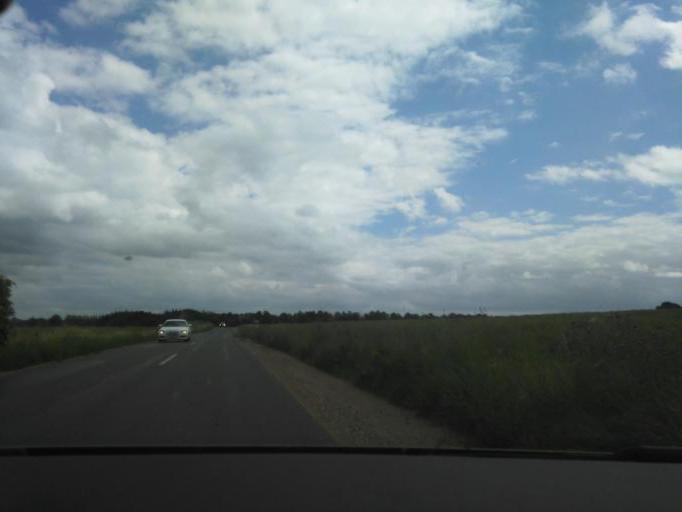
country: DK
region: Zealand
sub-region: Kalundborg Kommune
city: Gorlev
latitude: 55.5309
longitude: 11.1439
